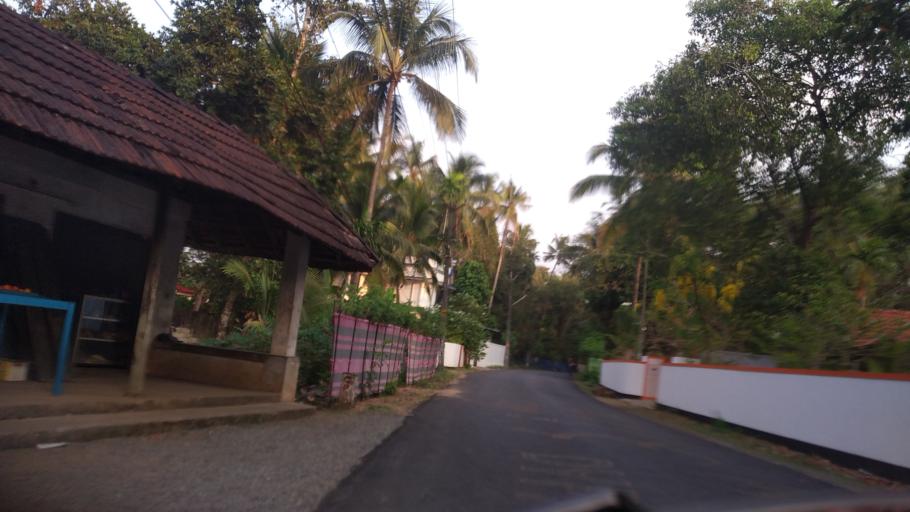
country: IN
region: Kerala
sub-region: Thrissur District
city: Thanniyam
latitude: 10.3560
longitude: 76.1115
